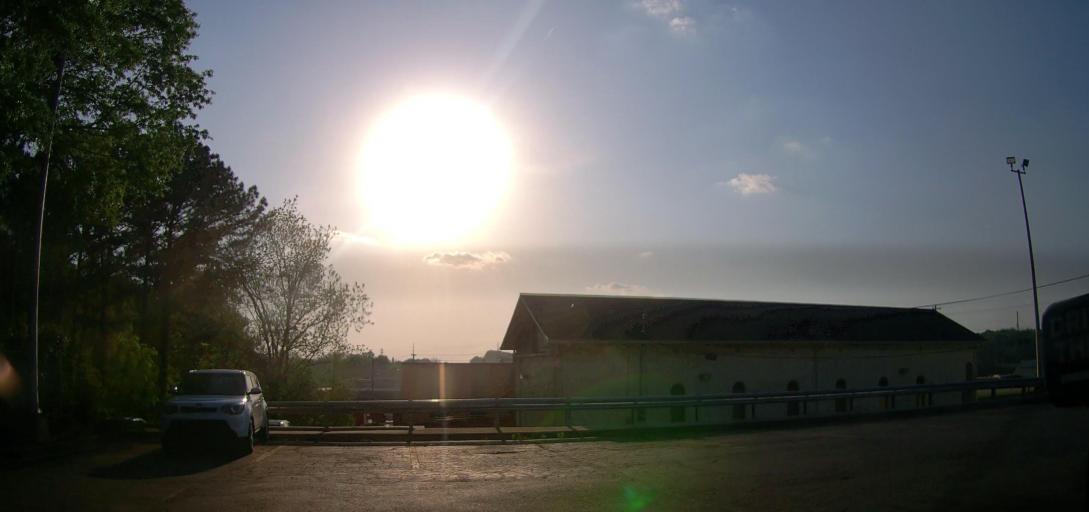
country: US
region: Georgia
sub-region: Newton County
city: Covington
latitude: 33.6023
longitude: -83.8549
